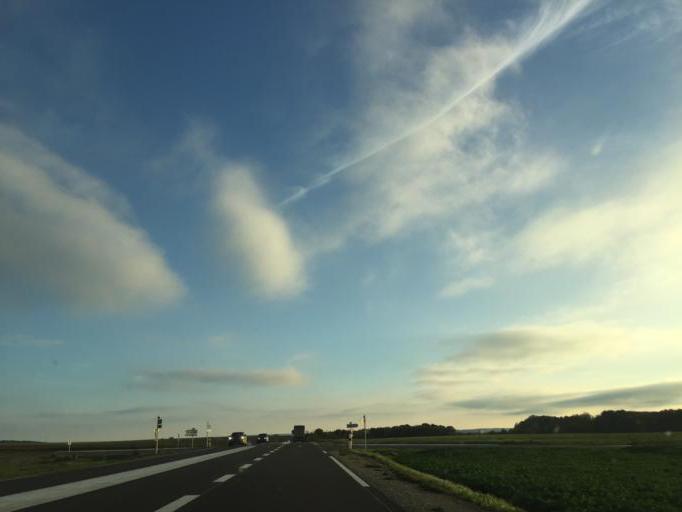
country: FR
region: Bourgogne
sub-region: Departement de l'Yonne
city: Sergines
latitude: 48.3469
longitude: 3.2315
